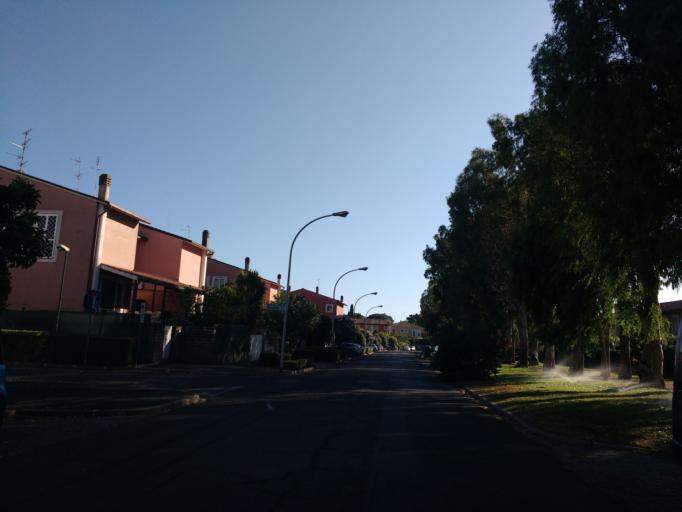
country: IT
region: Latium
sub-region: Citta metropolitana di Roma Capitale
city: Acilia-Castel Fusano-Ostia Antica
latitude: 41.7572
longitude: 12.3641
